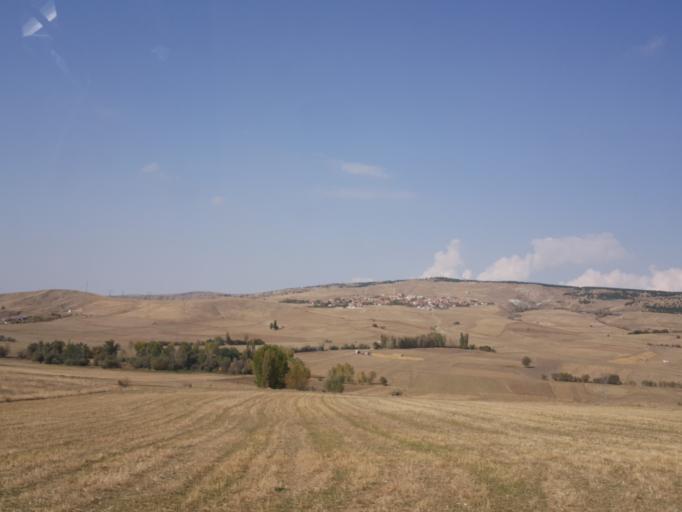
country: TR
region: Corum
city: Bogazkale
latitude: 40.1615
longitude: 34.6581
